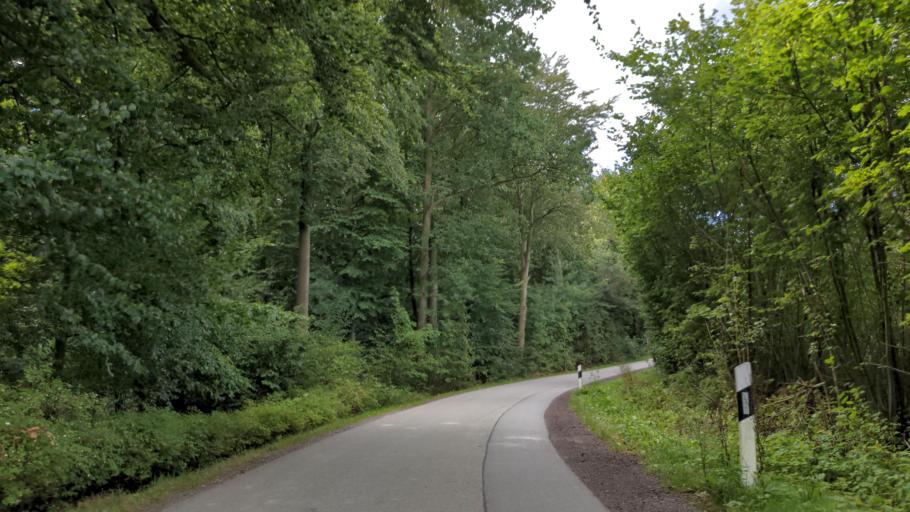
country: DE
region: Schleswig-Holstein
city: Kasseedorf
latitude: 54.1680
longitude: 10.7032
